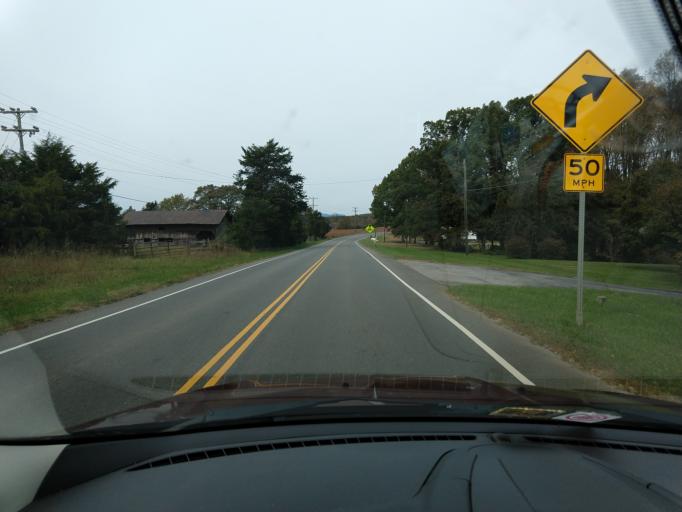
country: US
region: Virginia
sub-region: Franklin County
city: Union Hall
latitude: 36.9969
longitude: -79.7709
